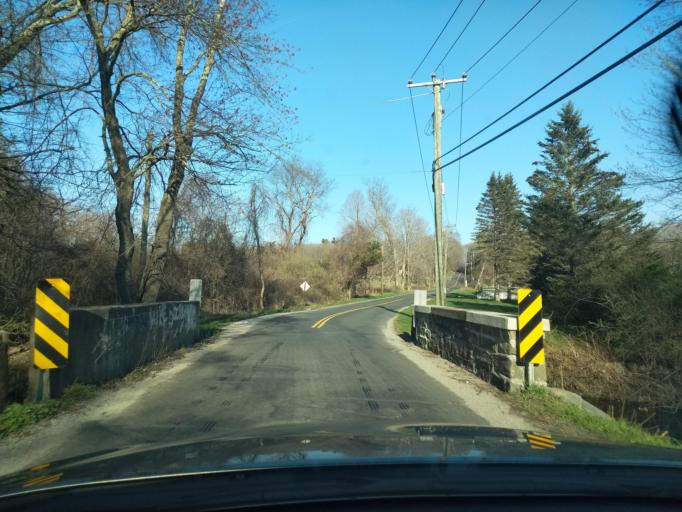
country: US
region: Connecticut
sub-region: Fairfield County
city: Newtown
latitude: 41.3601
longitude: -73.2822
